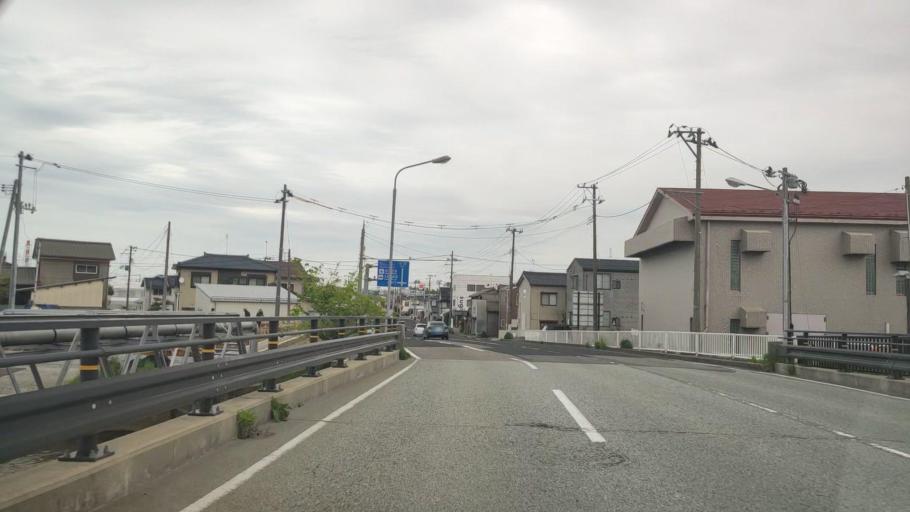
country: JP
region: Niigata
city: Niigata-shi
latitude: 37.9319
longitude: 139.0706
